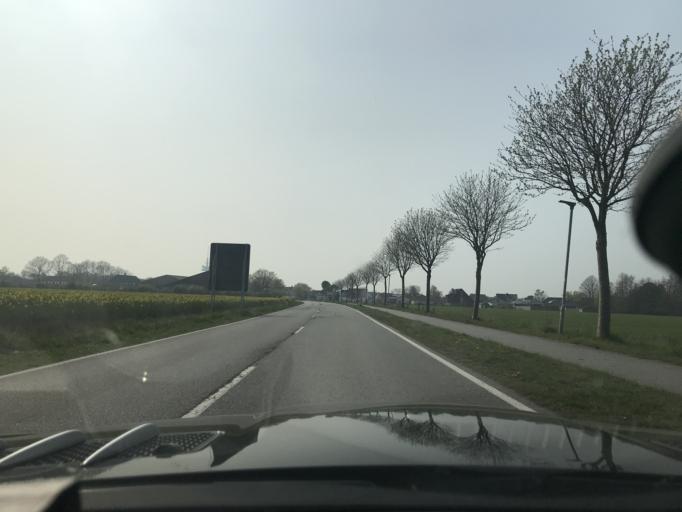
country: DE
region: Schleswig-Holstein
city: Fehmarn
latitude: 54.4967
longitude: 11.2186
